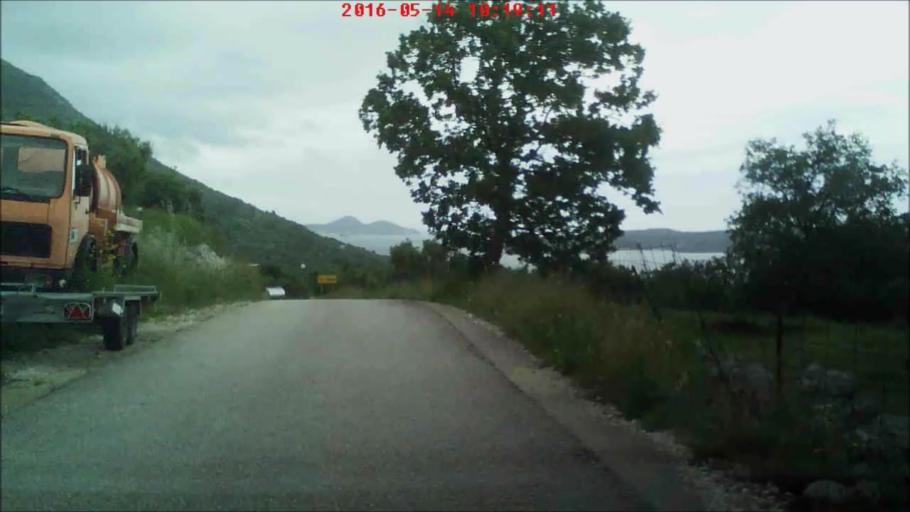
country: HR
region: Dubrovacko-Neretvanska
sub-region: Grad Dubrovnik
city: Mokosica
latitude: 42.7173
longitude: 17.9697
